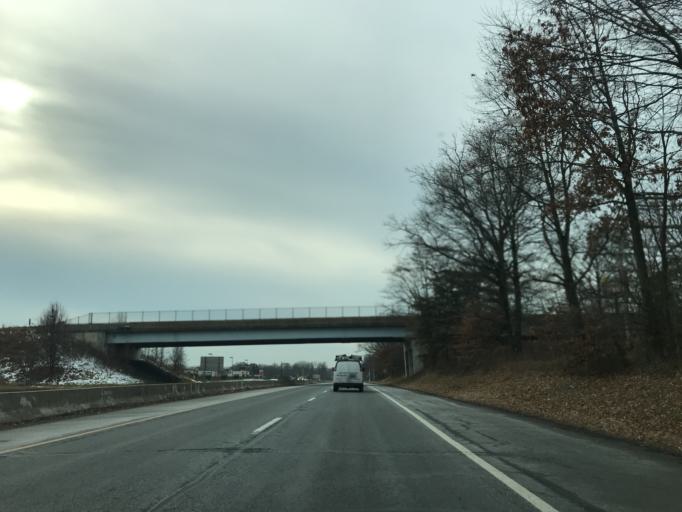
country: US
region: Maryland
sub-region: Harford County
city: Riverside
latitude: 39.4716
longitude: -76.2333
